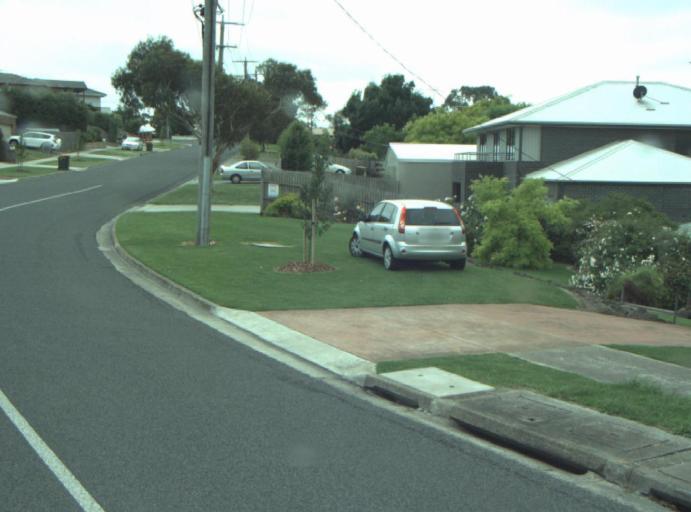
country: AU
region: Victoria
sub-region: Greater Geelong
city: Wandana Heights
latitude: -38.1788
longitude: 144.3049
